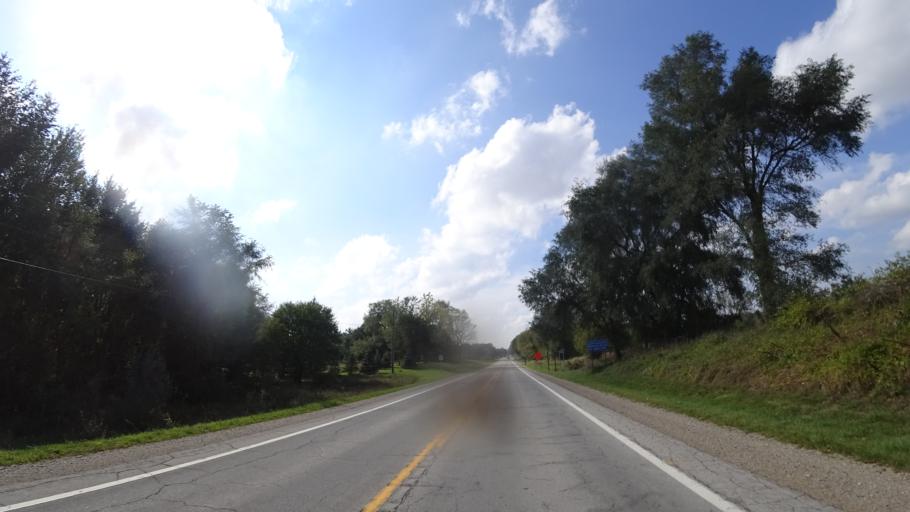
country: US
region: Michigan
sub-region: Saint Joseph County
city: Colon
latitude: 42.0102
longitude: -85.4059
